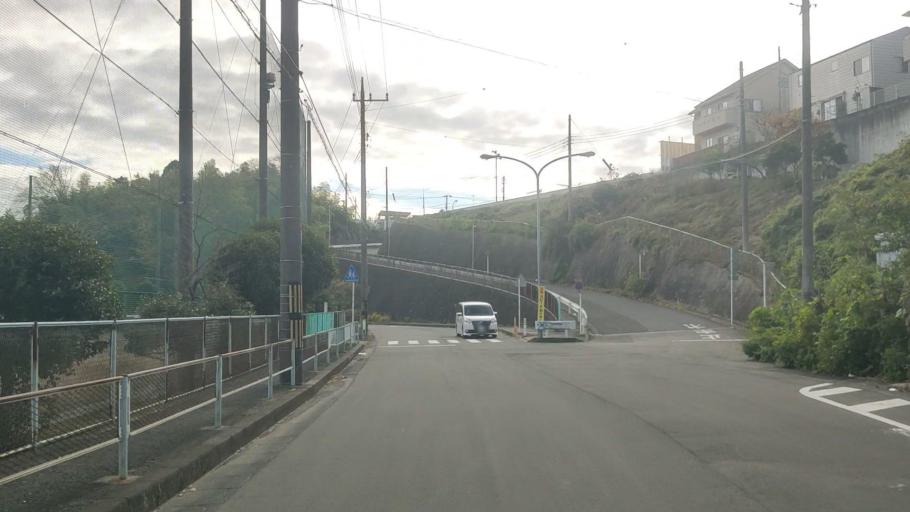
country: JP
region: Kanagawa
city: Minami-rinkan
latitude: 35.4792
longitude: 139.4680
